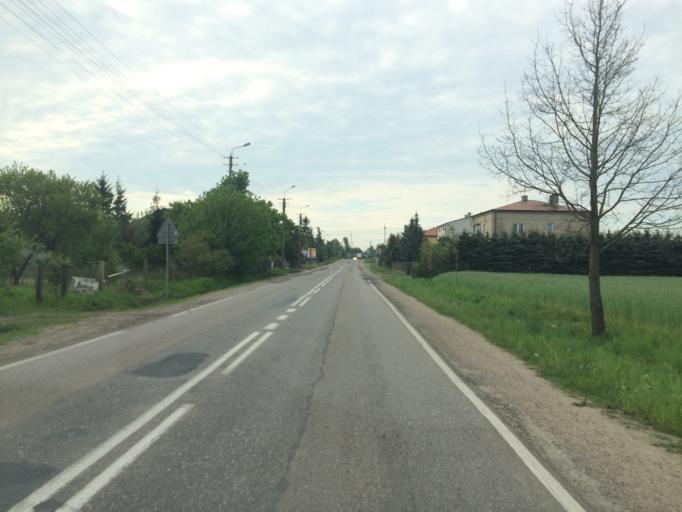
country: PL
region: Masovian Voivodeship
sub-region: Powiat mlawski
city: Mlawa
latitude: 53.1318
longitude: 20.3445
